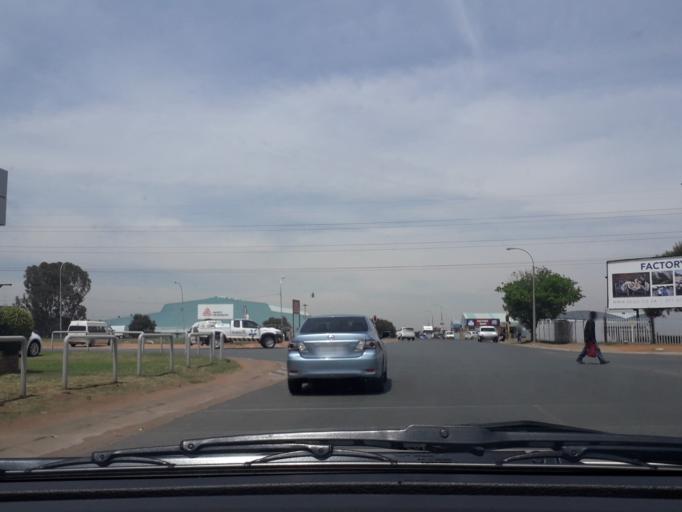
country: ZA
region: Gauteng
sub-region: City of Johannesburg Metropolitan Municipality
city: Roodepoort
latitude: -26.1917
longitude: 27.9234
